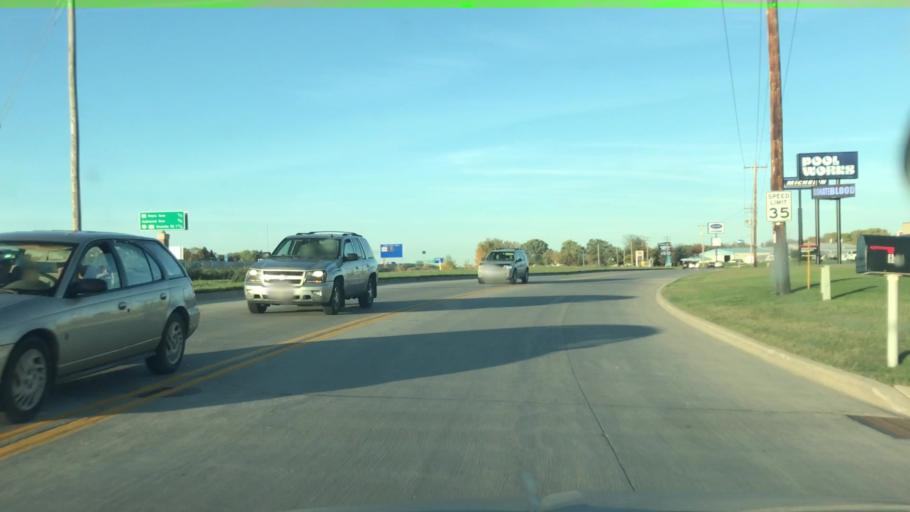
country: US
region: Wisconsin
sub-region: Brown County
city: De Pere
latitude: 44.4415
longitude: -88.0969
